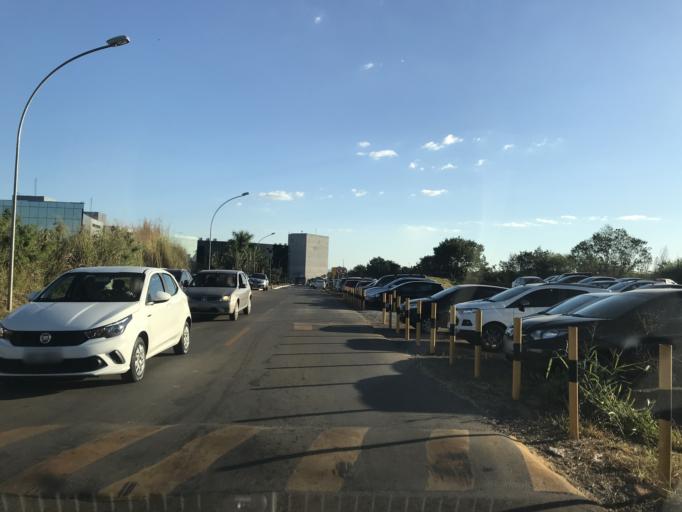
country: BR
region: Federal District
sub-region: Brasilia
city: Brasilia
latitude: -15.8087
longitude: -47.8443
